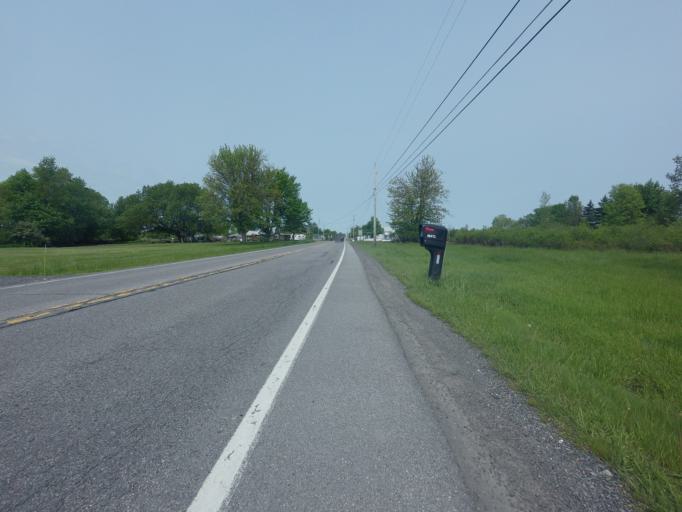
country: US
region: New York
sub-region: Jefferson County
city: Dexter
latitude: 44.0273
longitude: -76.0423
